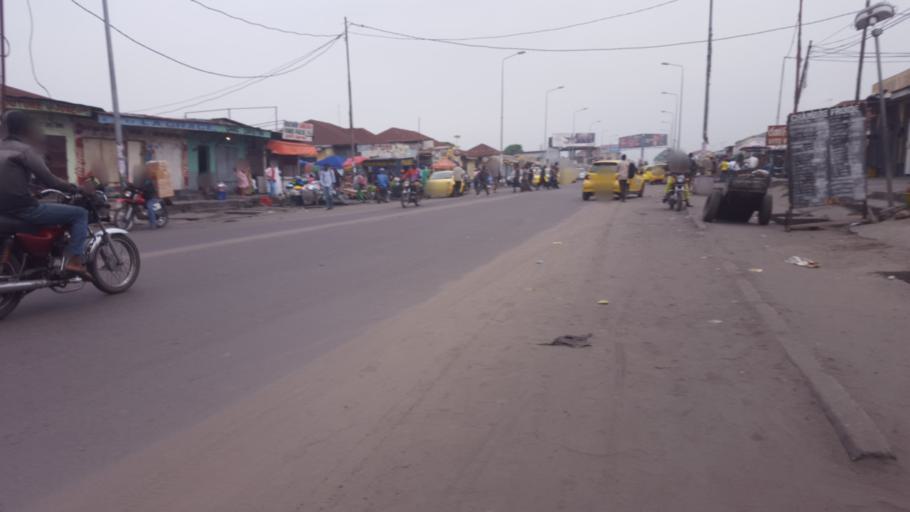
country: CD
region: Kinshasa
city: Kinshasa
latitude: -4.3402
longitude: 15.3120
